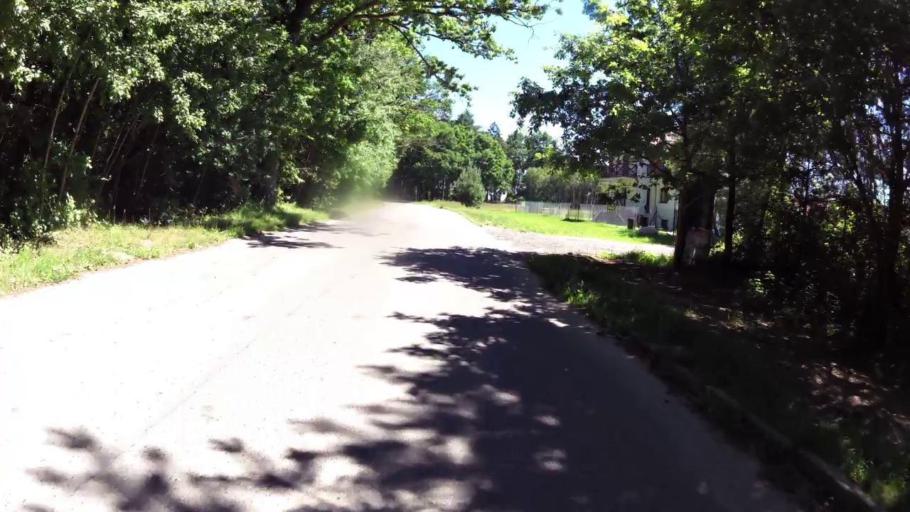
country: PL
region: West Pomeranian Voivodeship
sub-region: Powiat gryficki
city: Rewal
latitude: 54.0909
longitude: 15.0546
